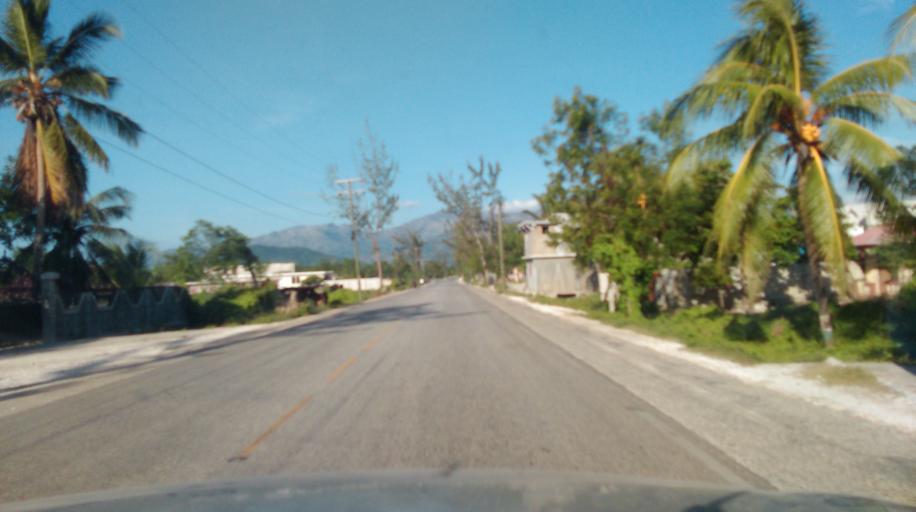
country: HT
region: Sud
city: Aquin
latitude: 18.3072
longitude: -73.3190
